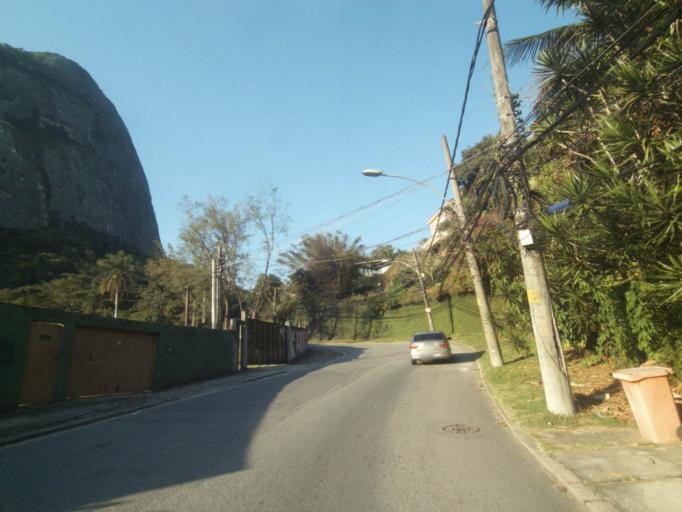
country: BR
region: Rio de Janeiro
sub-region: Rio De Janeiro
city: Rio de Janeiro
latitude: -23.0086
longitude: -43.2895
